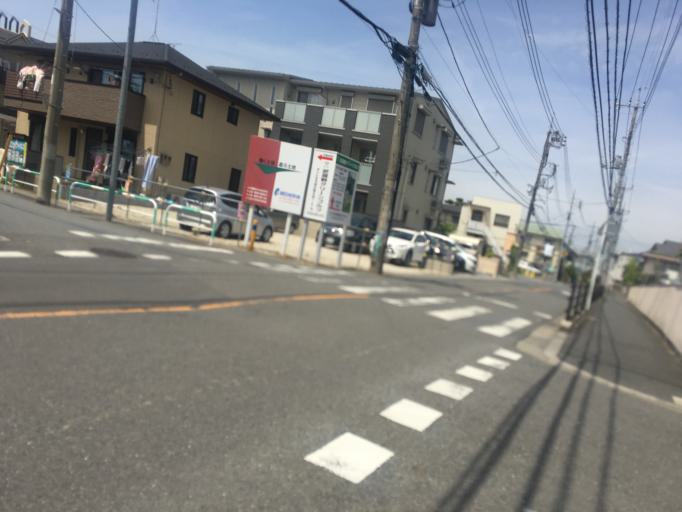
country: JP
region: Saitama
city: Yono
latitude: 35.8461
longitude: 139.6374
